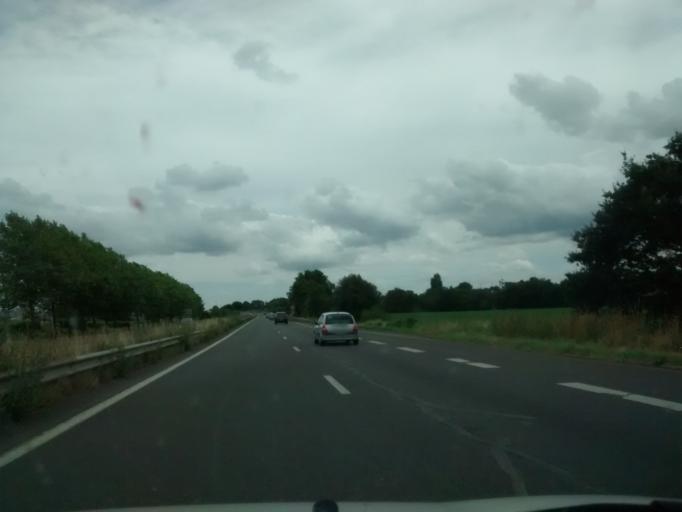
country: FR
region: Brittany
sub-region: Departement des Cotes-d'Armor
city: Lamballe
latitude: 48.4650
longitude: -2.5452
